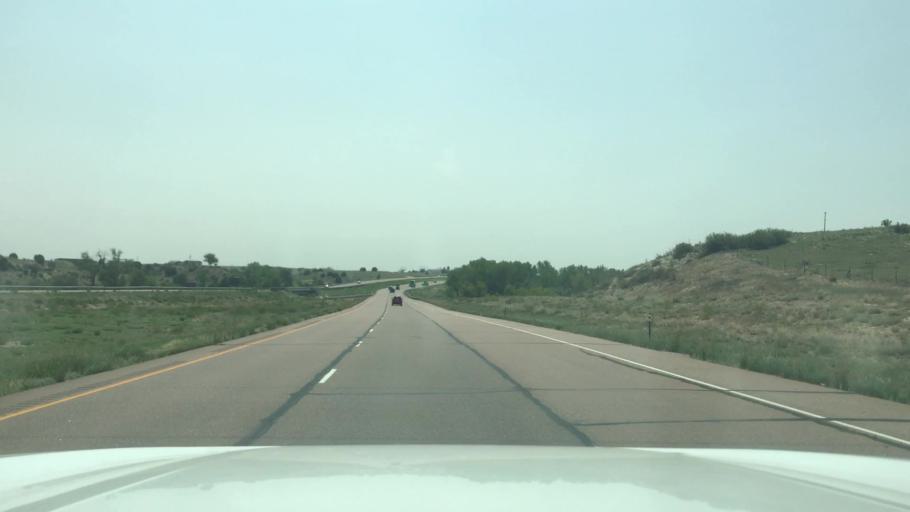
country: US
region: Colorado
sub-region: Pueblo County
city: Pueblo
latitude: 38.1238
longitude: -104.6712
